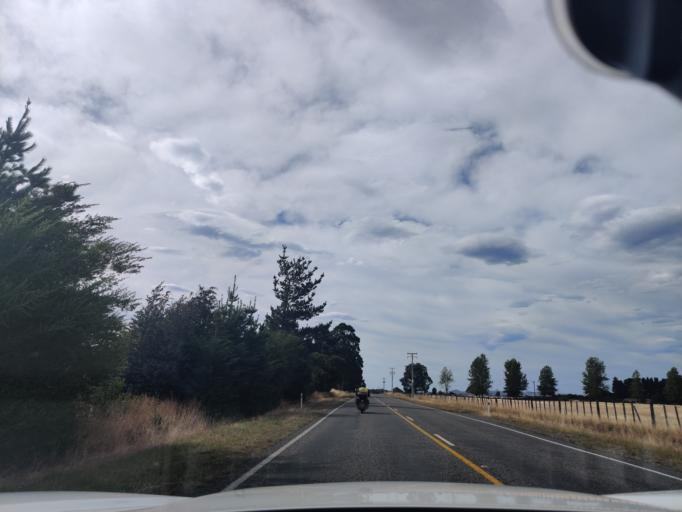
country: NZ
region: Wellington
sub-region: Masterton District
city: Masterton
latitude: -40.8738
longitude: 175.6512
